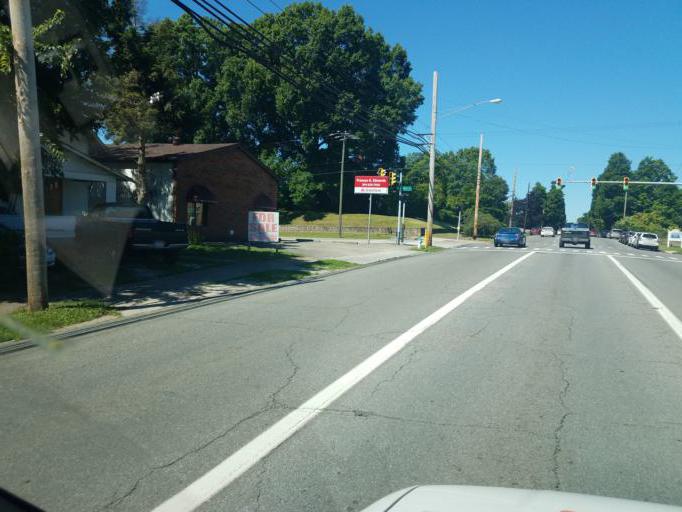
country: US
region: West Virginia
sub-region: Cabell County
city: Huntington
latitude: 38.4293
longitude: -82.4022
